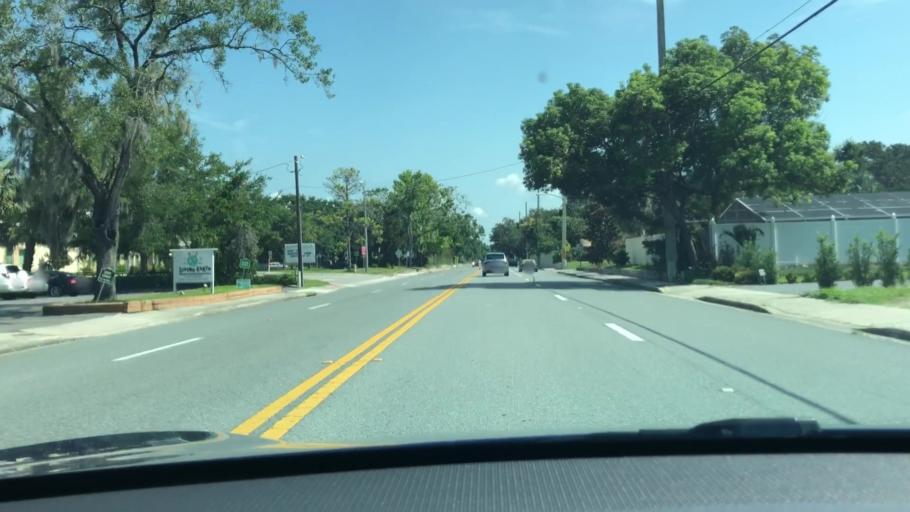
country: US
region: Florida
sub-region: Orange County
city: Winter Park
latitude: 28.6059
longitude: -81.3281
